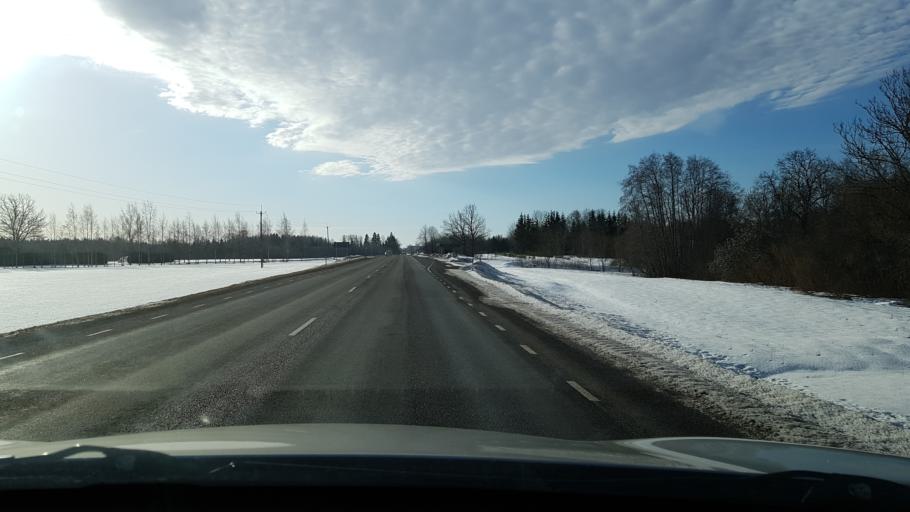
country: EE
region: Viljandimaa
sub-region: Viljandi linn
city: Viljandi
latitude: 58.4437
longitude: 25.5955
